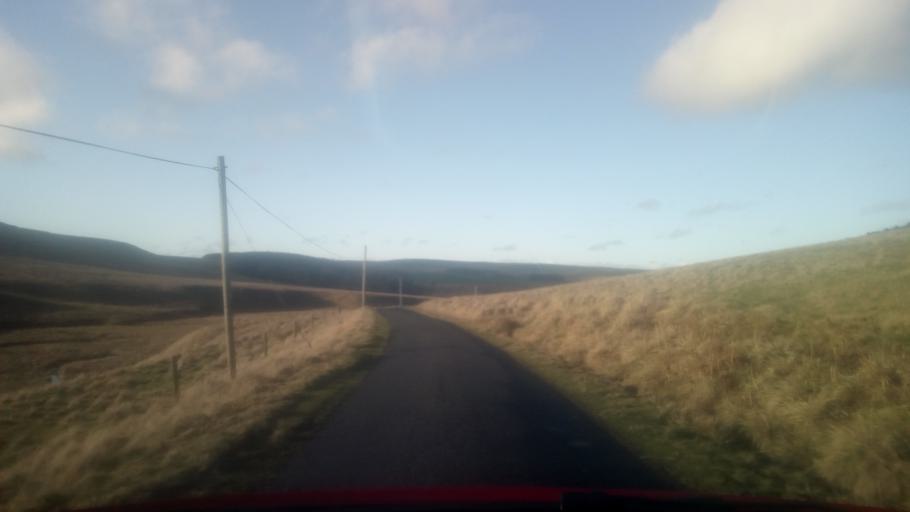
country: GB
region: England
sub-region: Northumberland
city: Rochester
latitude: 55.4063
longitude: -2.3787
